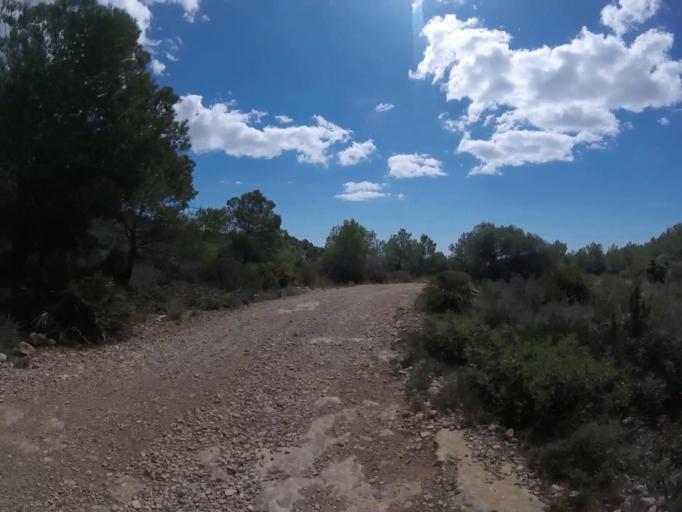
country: ES
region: Valencia
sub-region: Provincia de Castello
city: Alcoceber
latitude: 40.2901
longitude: 0.3169
